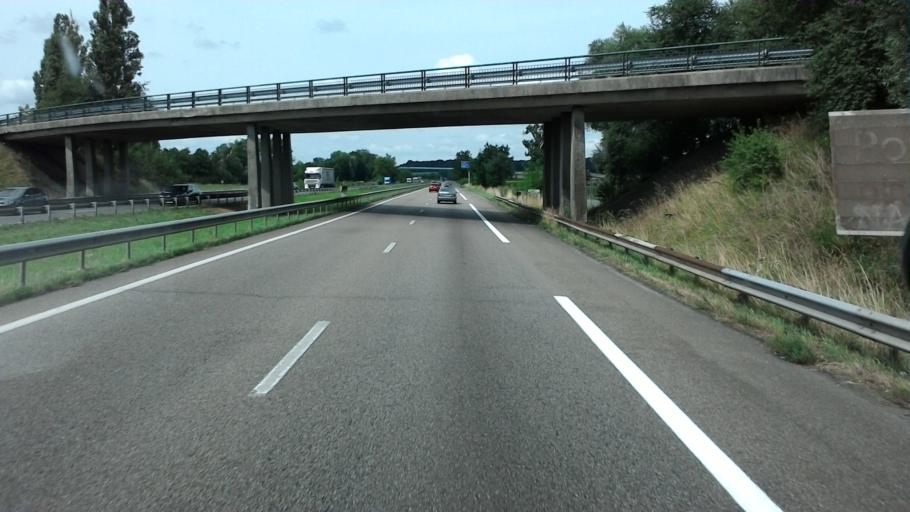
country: FR
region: Lorraine
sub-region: Departement de Meurthe-et-Moselle
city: Dieulouard
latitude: 48.8681
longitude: 6.0939
